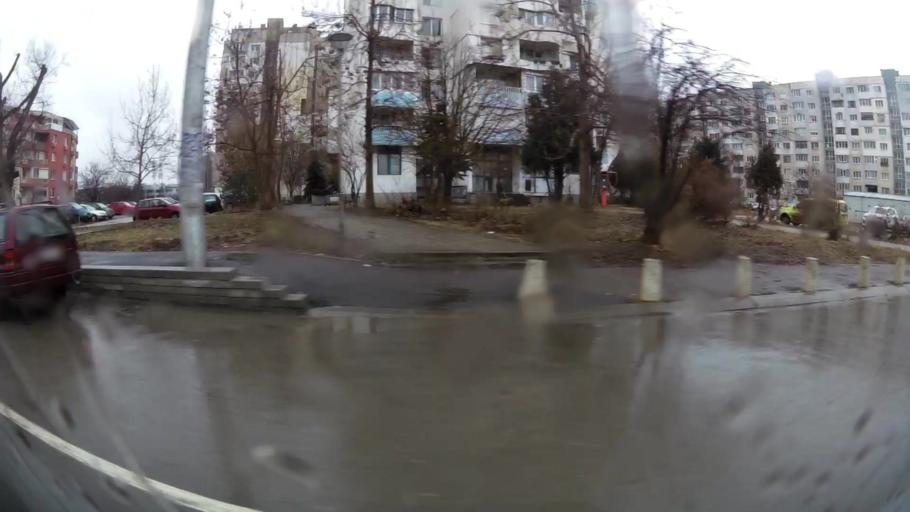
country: BG
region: Sofia-Capital
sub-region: Stolichna Obshtina
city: Sofia
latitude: 42.6498
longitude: 23.4050
